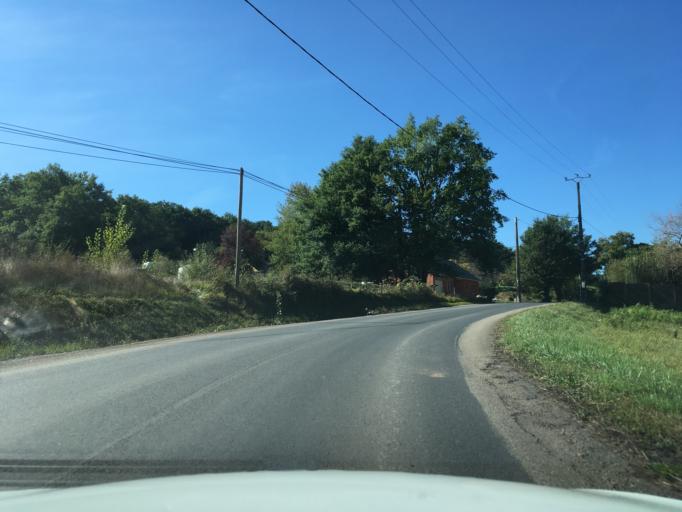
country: FR
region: Limousin
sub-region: Departement de la Correze
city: Saint-Pantaleon-de-Larche
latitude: 45.1369
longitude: 1.4810
